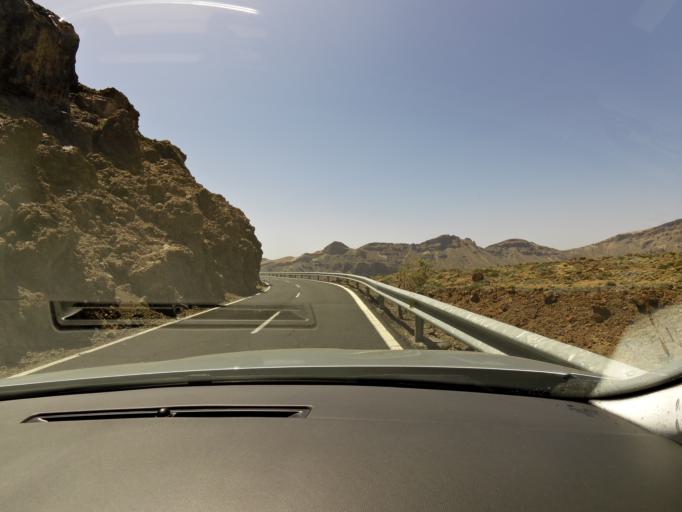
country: ES
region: Canary Islands
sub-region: Provincia de Santa Cruz de Tenerife
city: Los Realejos
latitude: 28.2614
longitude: -16.5959
